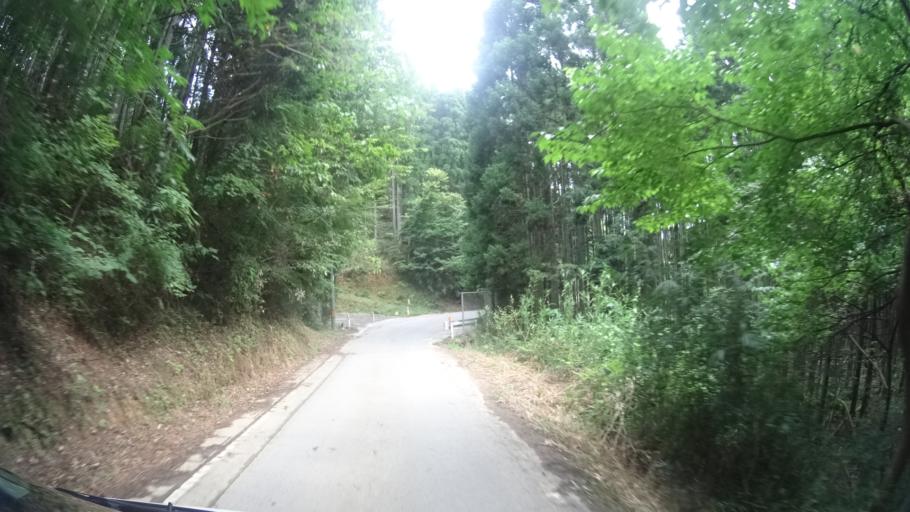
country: JP
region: Kyoto
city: Maizuru
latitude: 35.3518
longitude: 135.3471
